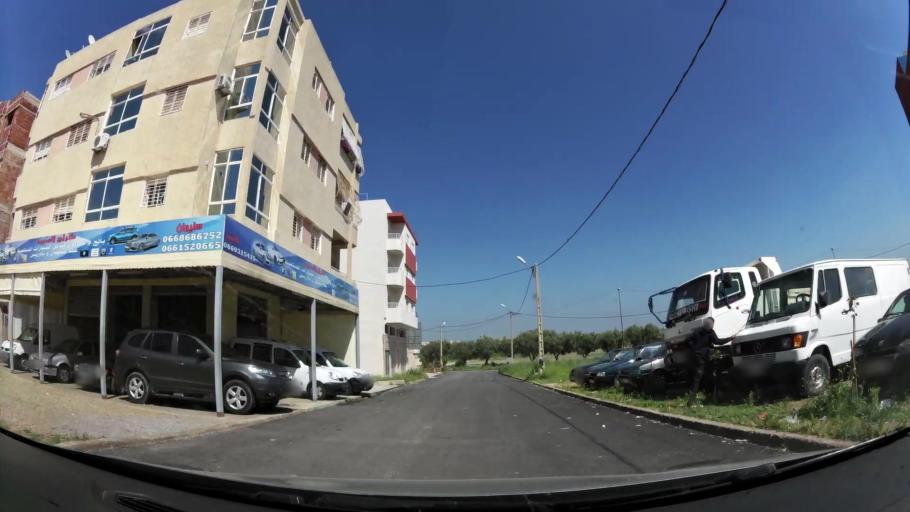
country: MA
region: Fes-Boulemane
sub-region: Fes
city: Fes
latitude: 34.0065
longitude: -5.0327
